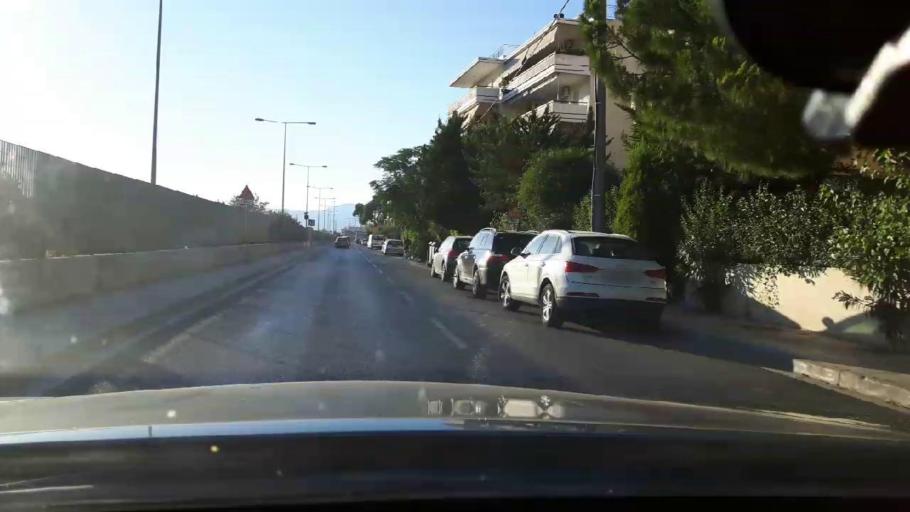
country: GR
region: Attica
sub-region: Nomarchia Athinas
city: Vrilissia
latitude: 38.0299
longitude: 23.8265
